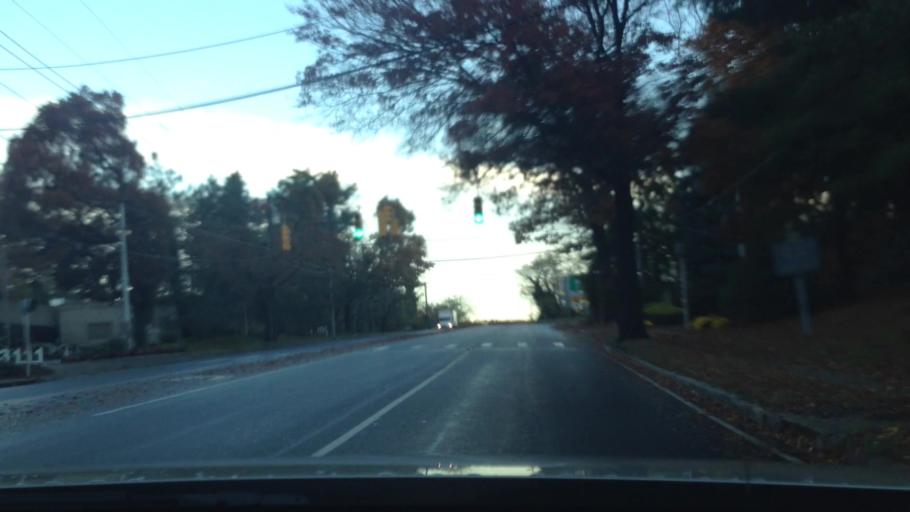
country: US
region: New York
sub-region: Nassau County
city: Manhasset Hills
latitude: 40.7637
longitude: -73.6897
